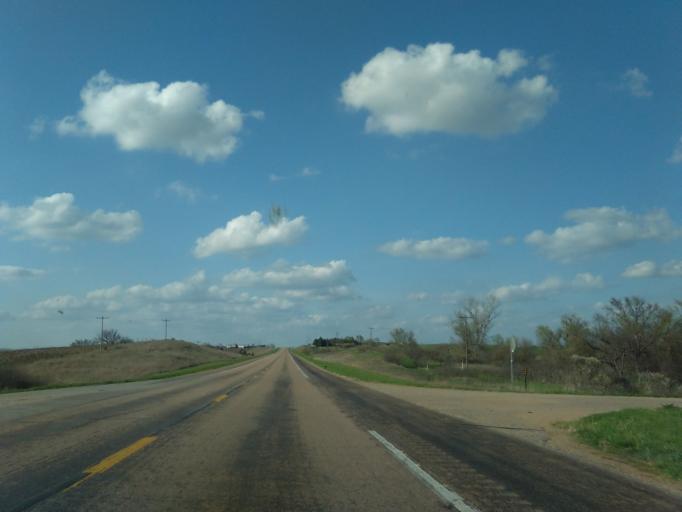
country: US
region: Nebraska
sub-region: Webster County
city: Red Cloud
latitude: 40.1320
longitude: -98.5189
